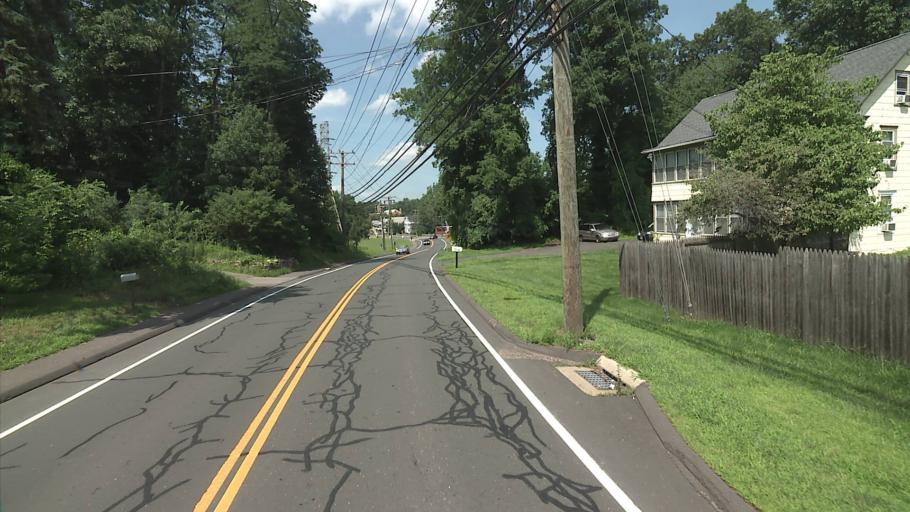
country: US
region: Connecticut
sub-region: Tolland County
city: Rockville
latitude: 41.8647
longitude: -72.4655
